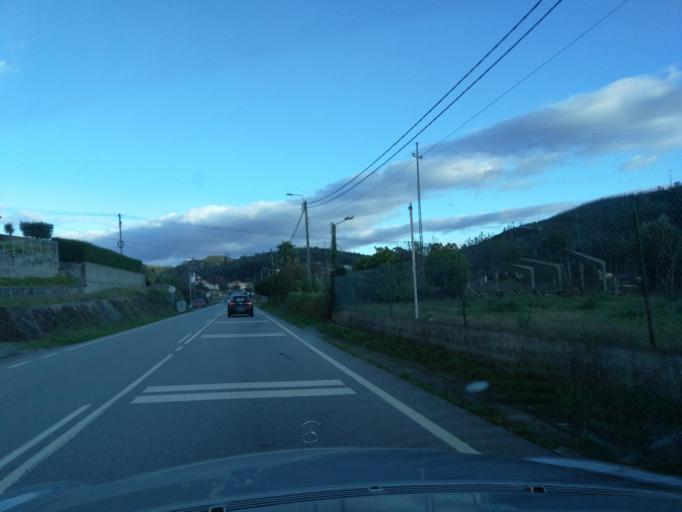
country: PT
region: Braga
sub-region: Barcelos
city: Vila Frescainha
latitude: 41.5724
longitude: -8.6931
